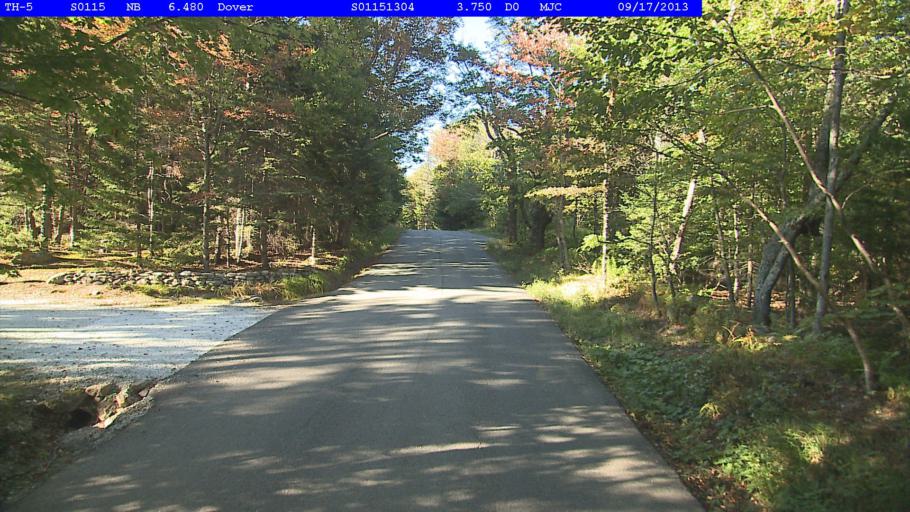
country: US
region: Vermont
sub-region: Windham County
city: Dover
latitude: 42.9773
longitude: -72.8930
